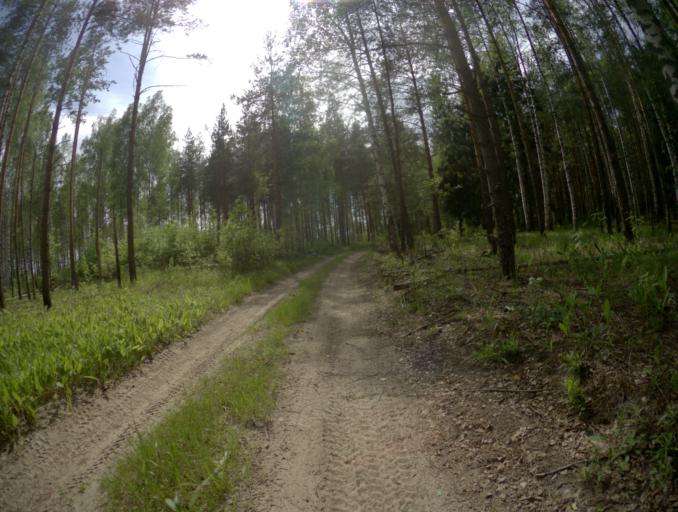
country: RU
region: Vladimir
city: Ivanishchi
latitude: 55.7200
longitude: 40.3685
